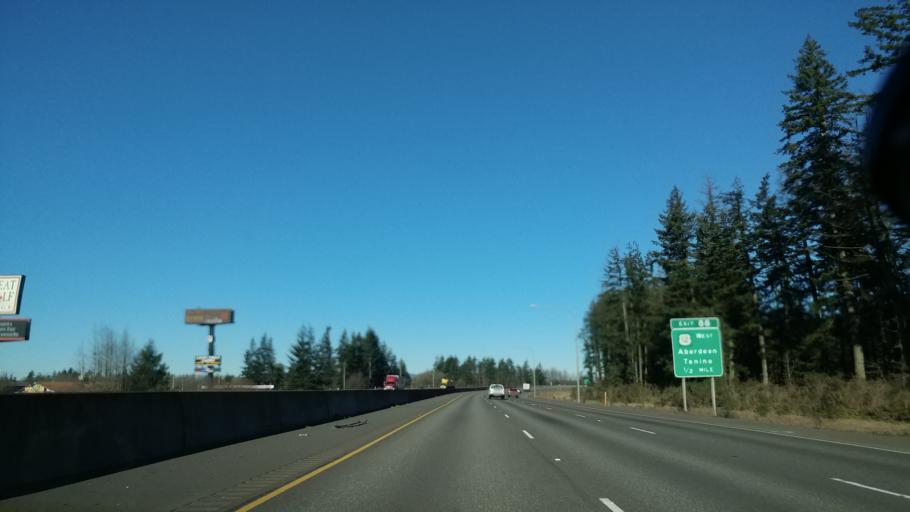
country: US
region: Washington
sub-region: Thurston County
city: Grand Mound
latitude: 46.7911
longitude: -123.0086
